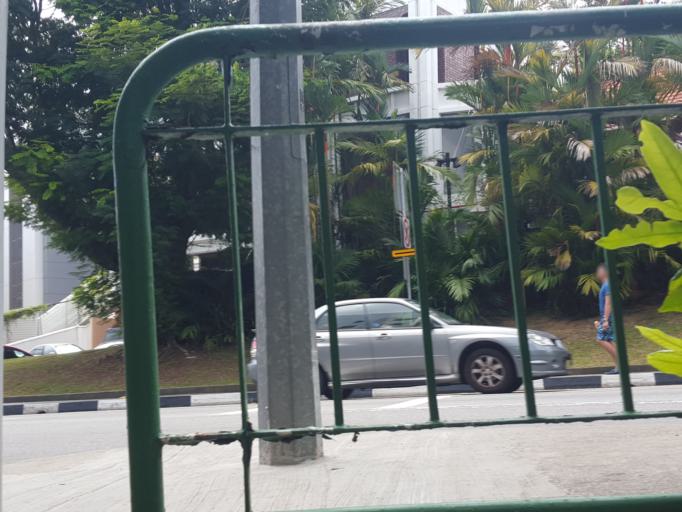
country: SG
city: Singapore
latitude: 1.2976
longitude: 103.8478
